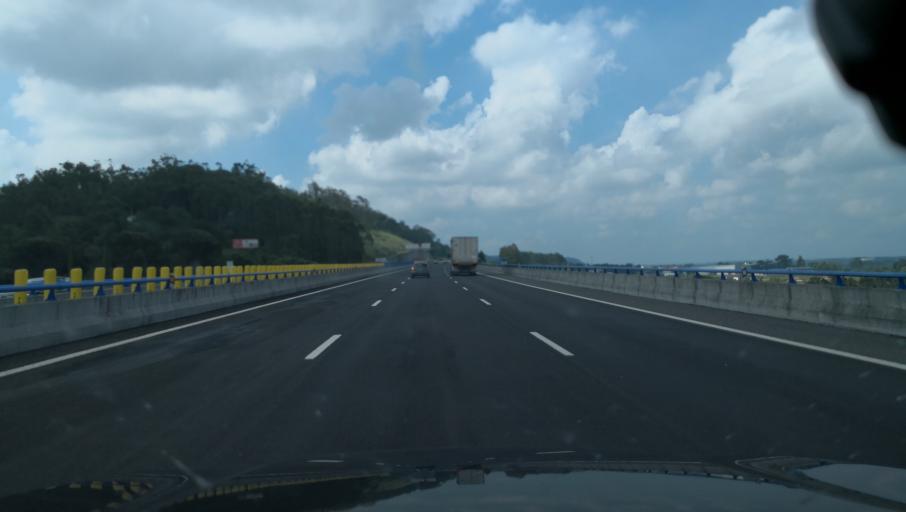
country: PT
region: Leiria
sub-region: Caldas da Rainha
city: Caldas da Rainha
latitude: 39.4955
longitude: -9.0926
